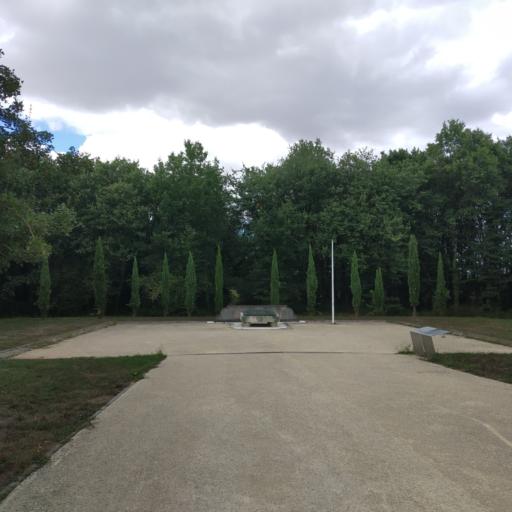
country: FR
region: Poitou-Charentes
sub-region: Departement de la Vienne
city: Biard
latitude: 46.5906
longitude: 0.2977
